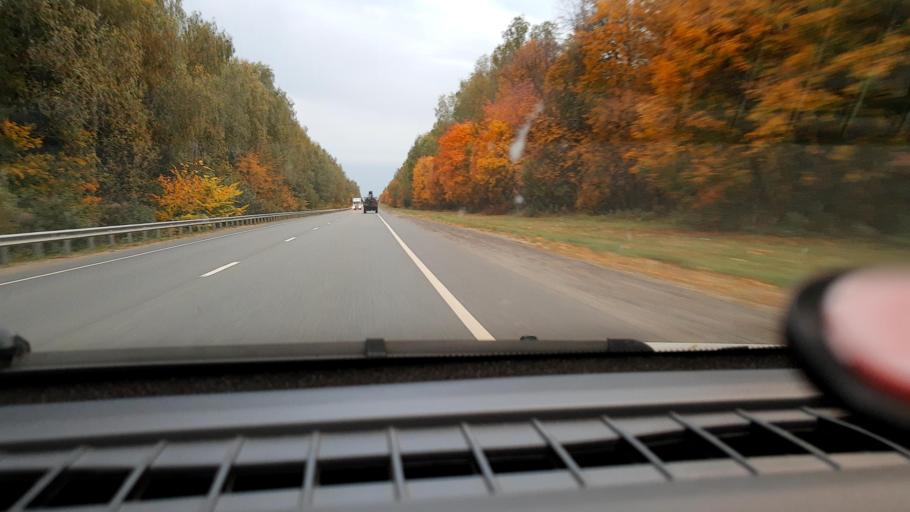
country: RU
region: Vladimir
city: Orgtrud
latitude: 56.1992
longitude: 40.8268
